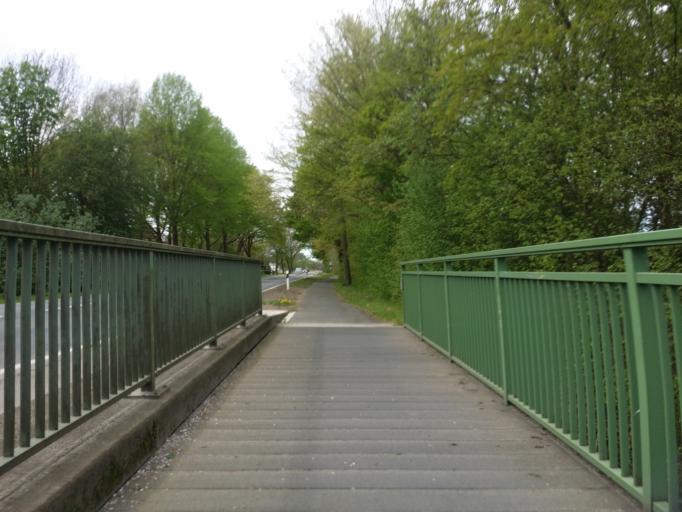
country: DE
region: Lower Saxony
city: Lemwerder
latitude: 53.1418
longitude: 8.5900
